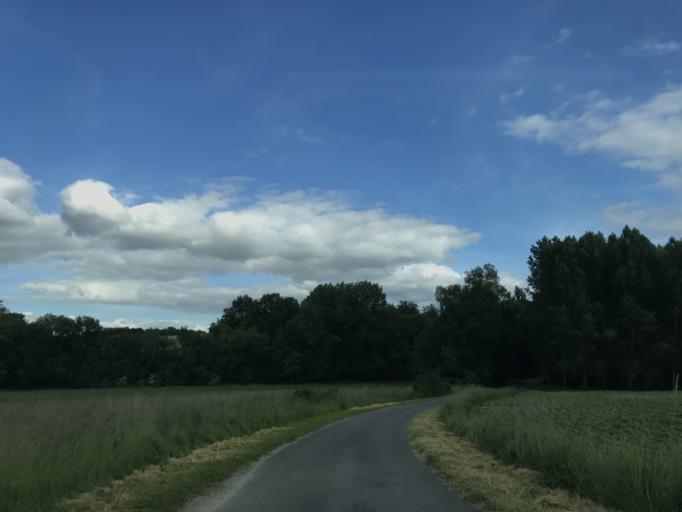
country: FR
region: Aquitaine
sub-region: Departement de la Dordogne
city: Saint-Aulaye
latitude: 45.2657
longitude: 0.1229
